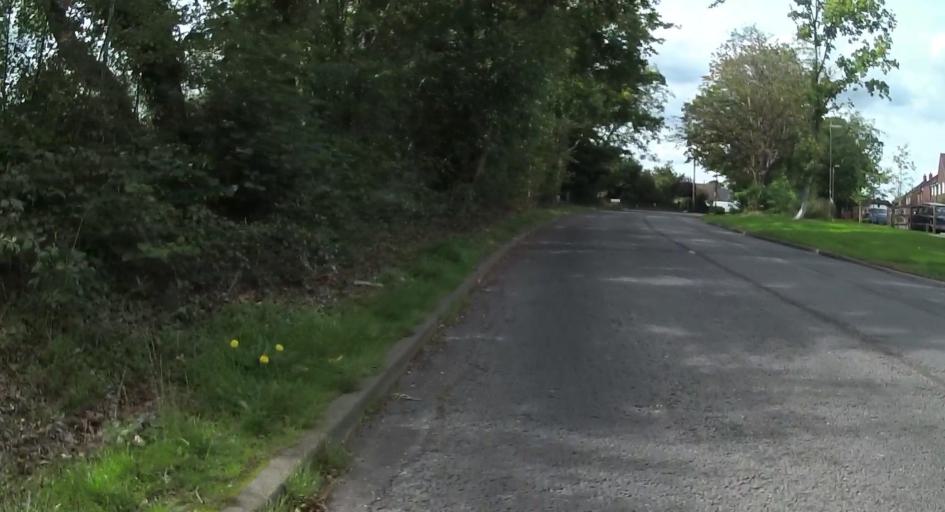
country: GB
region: England
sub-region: Surrey
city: Knaphill
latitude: 51.3371
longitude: -0.6333
